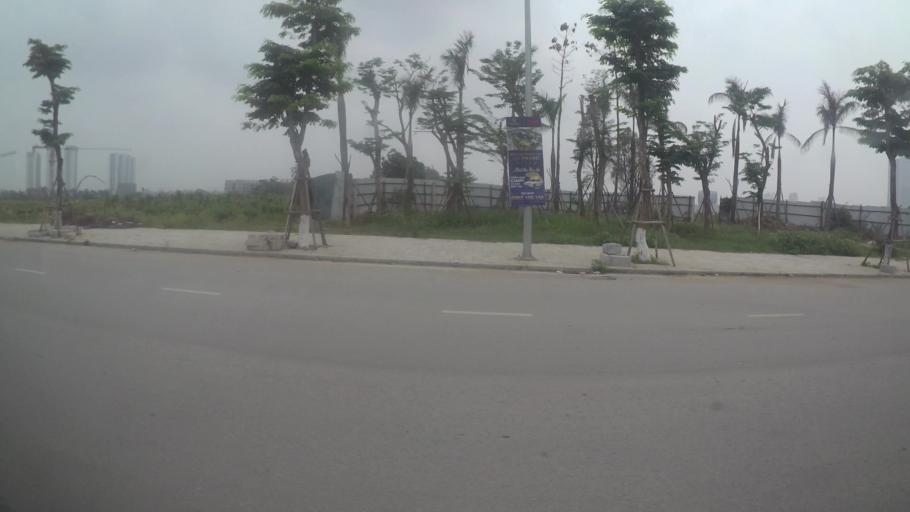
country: VN
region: Ha Noi
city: Ha Dong
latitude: 20.9818
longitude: 105.7589
